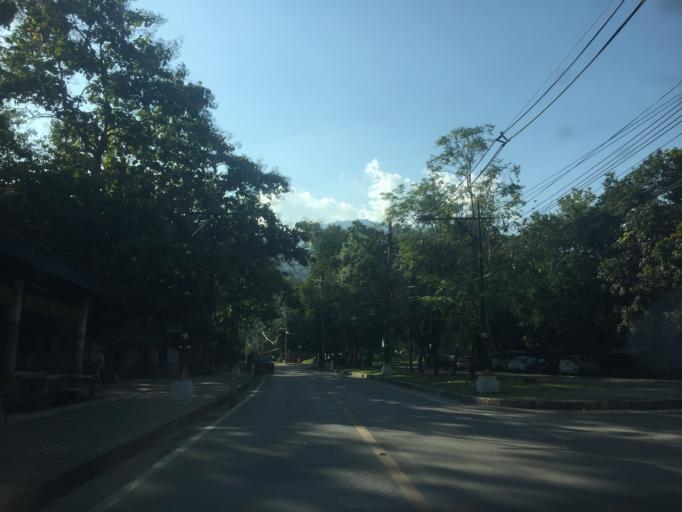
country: TH
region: Chiang Mai
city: Chiang Mai
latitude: 18.7995
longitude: 98.9493
